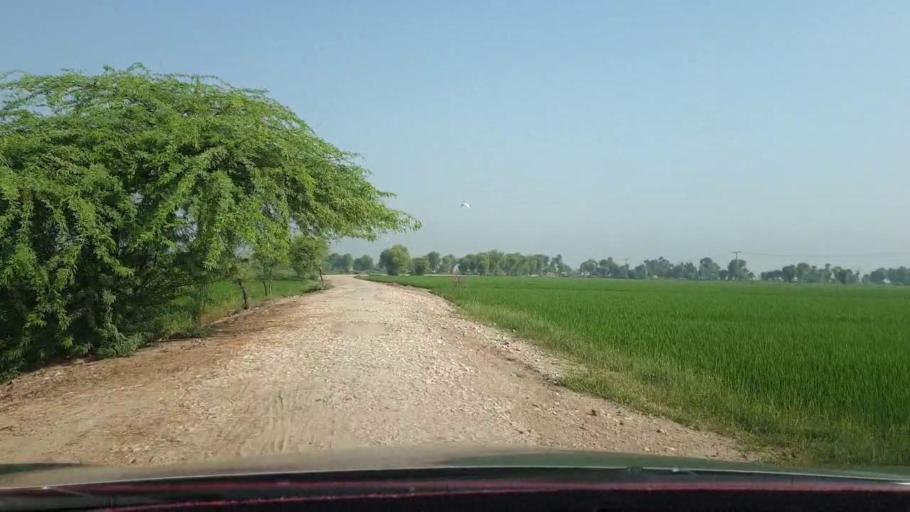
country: PK
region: Sindh
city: Nasirabad
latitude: 27.4452
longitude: 67.9193
